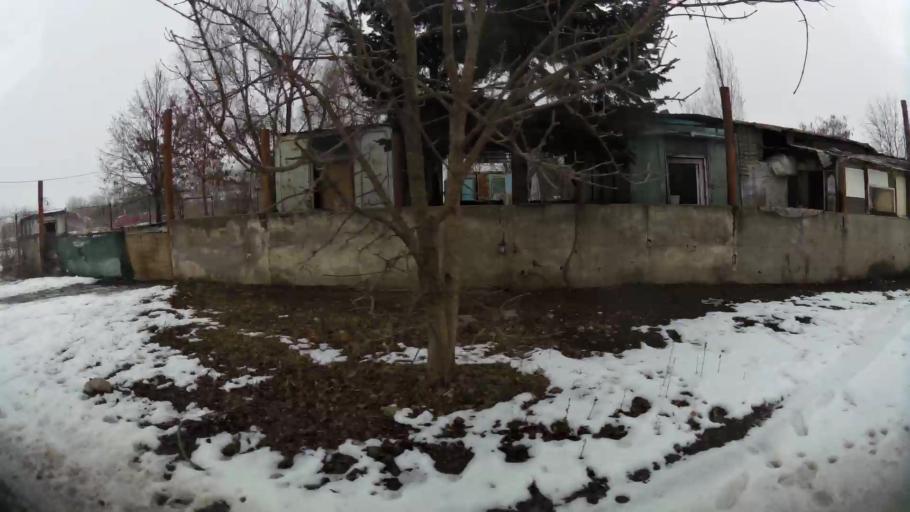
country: RO
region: Ilfov
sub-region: Comuna Chiajna
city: Rosu
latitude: 44.4478
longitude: 26.0256
